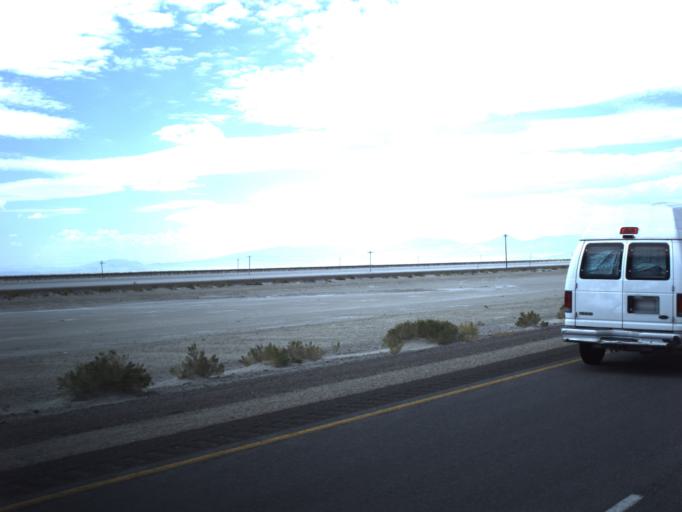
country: US
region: Utah
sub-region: Tooele County
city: Wendover
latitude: 40.7376
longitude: -113.7616
